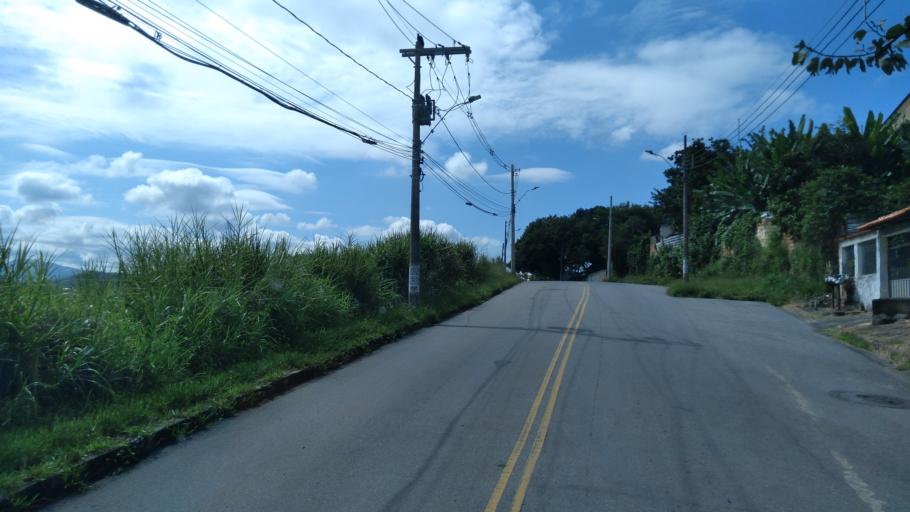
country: BR
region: Minas Gerais
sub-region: Santa Luzia
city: Santa Luzia
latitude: -19.8212
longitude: -43.9004
